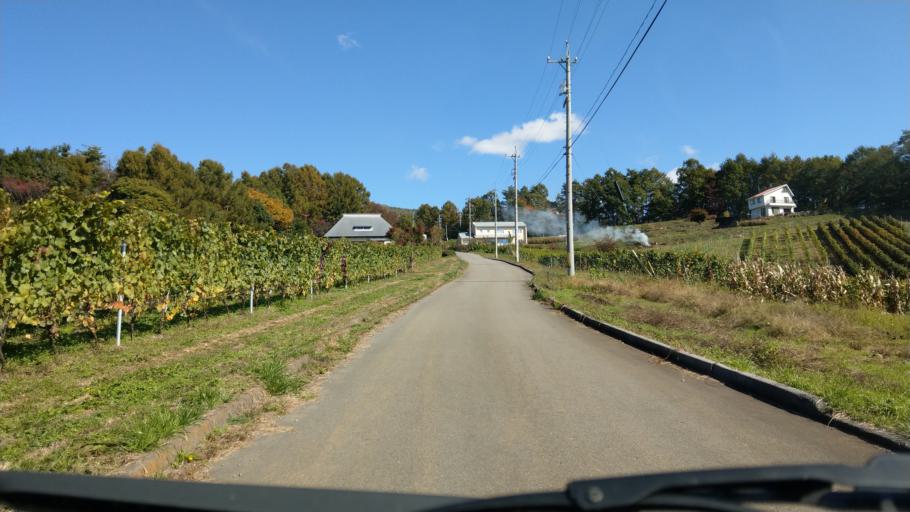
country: JP
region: Nagano
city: Komoro
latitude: 36.3650
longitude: 138.4057
